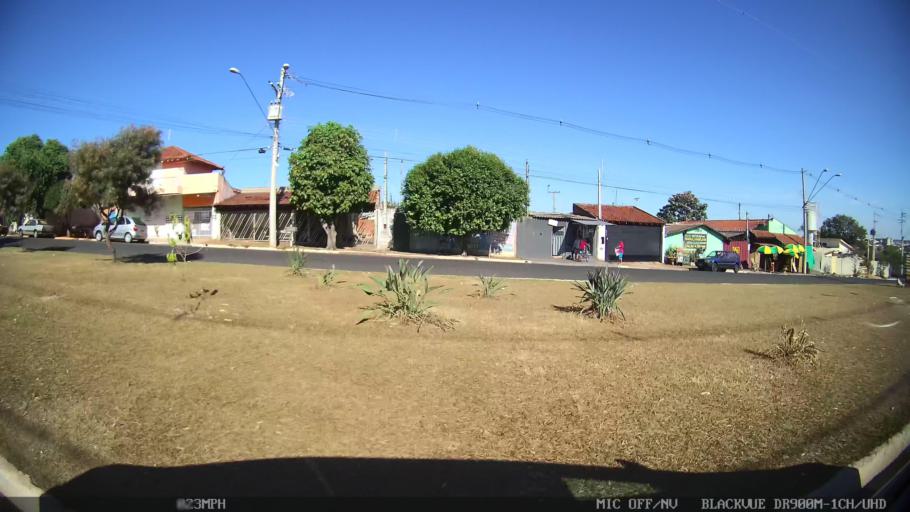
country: BR
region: Sao Paulo
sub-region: Olimpia
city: Olimpia
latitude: -20.7260
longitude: -48.9116
